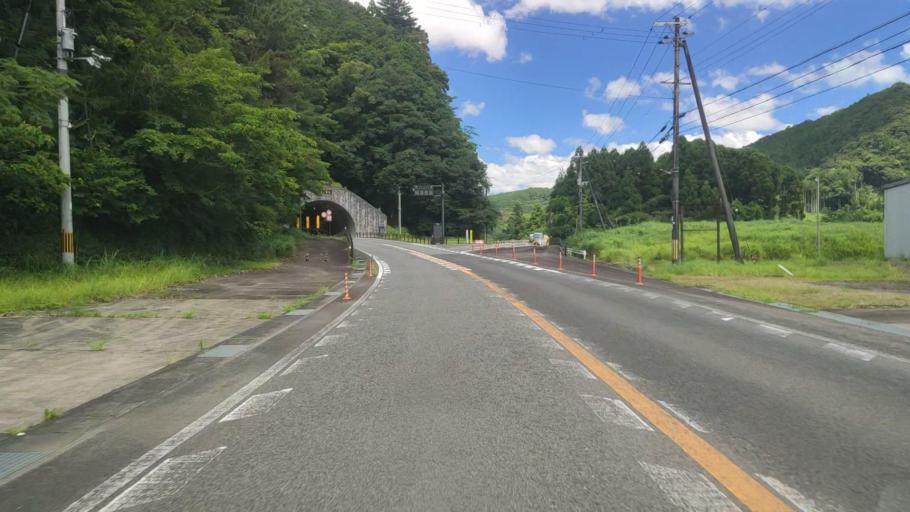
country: JP
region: Wakayama
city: Shingu
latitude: 33.8004
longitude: 135.8876
